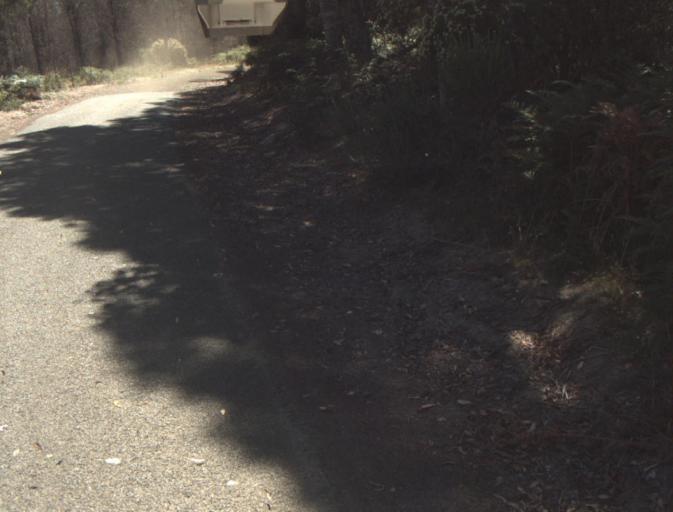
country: AU
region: Tasmania
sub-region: Dorset
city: Scottsdale
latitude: -41.2738
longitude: 147.3437
